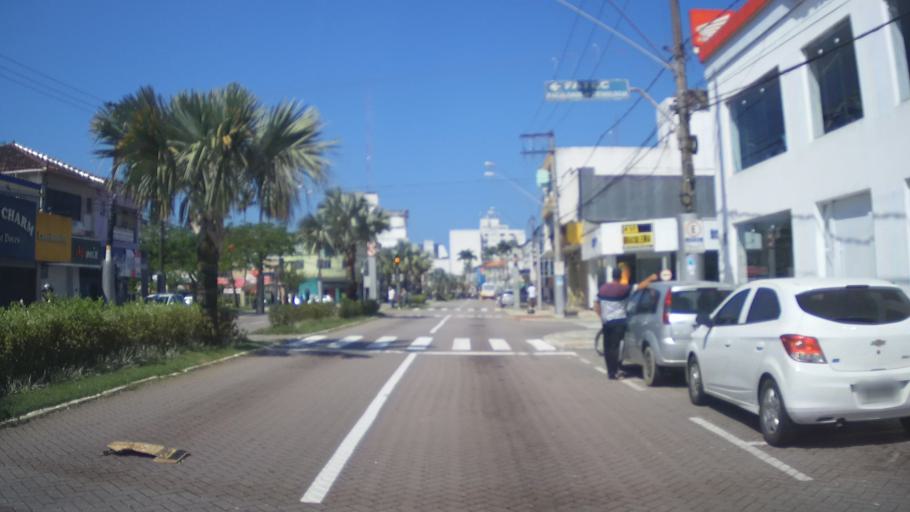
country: BR
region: Sao Paulo
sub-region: Praia Grande
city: Praia Grande
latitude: -24.0043
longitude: -46.4132
